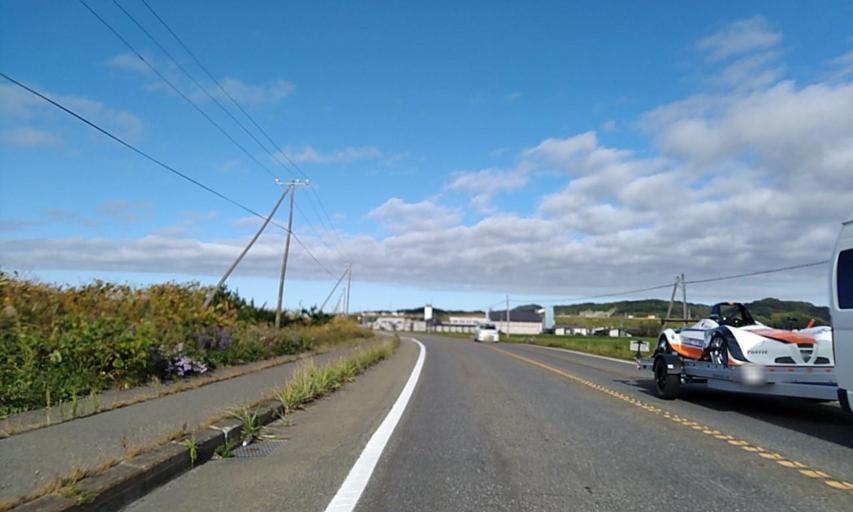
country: JP
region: Hokkaido
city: Shizunai-furukawacho
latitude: 42.2441
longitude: 142.5852
